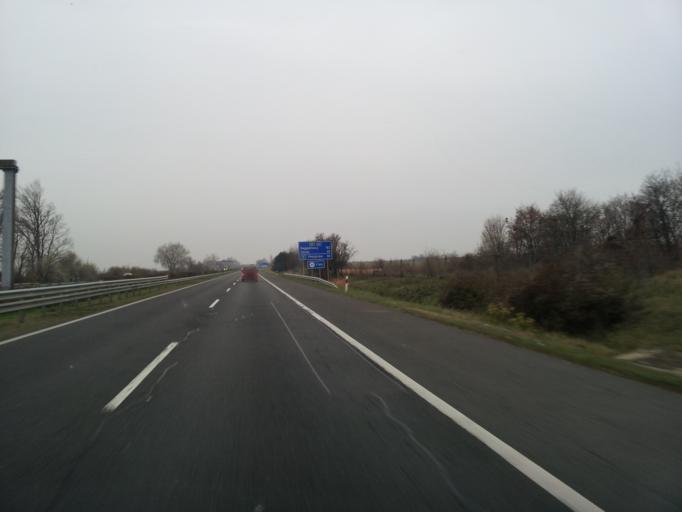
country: HU
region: Fejer
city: Pakozd
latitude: 47.1896
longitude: 18.5029
